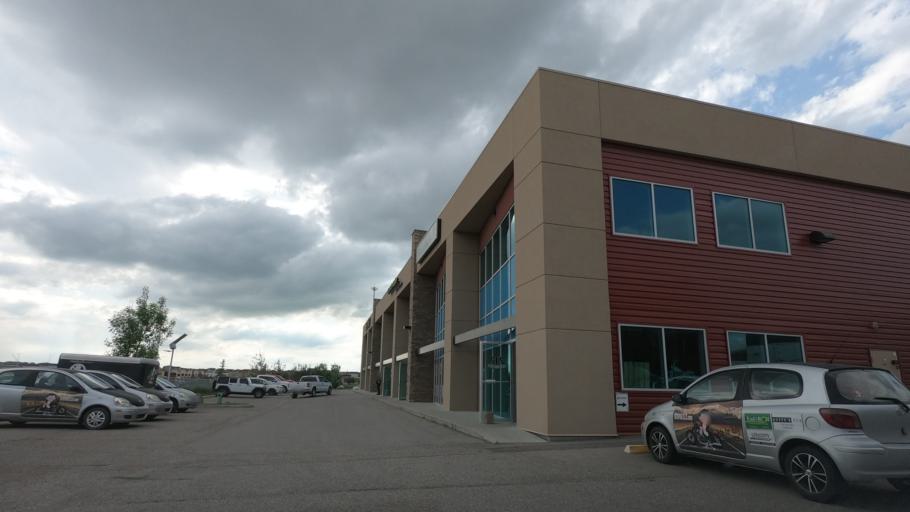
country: CA
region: Alberta
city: Airdrie
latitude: 51.2591
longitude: -113.9982
